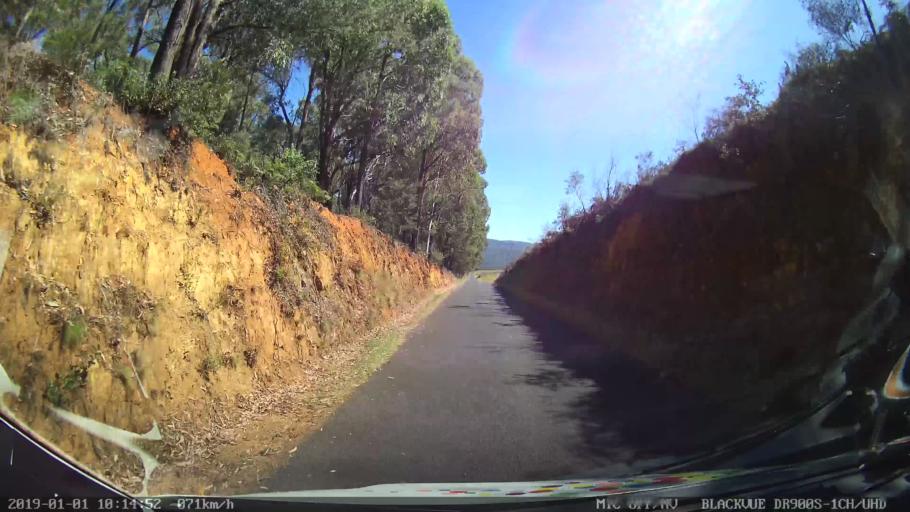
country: AU
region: New South Wales
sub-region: Snowy River
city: Jindabyne
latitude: -36.1079
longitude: 148.1616
